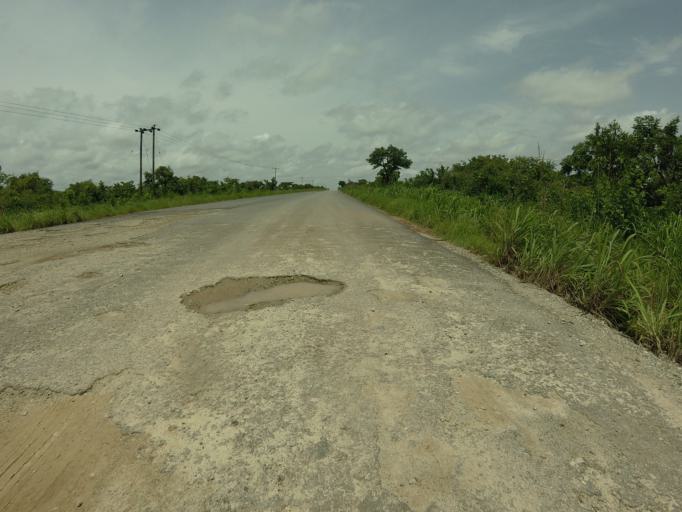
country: GH
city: Kpandae
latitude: 8.5688
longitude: 0.2486
